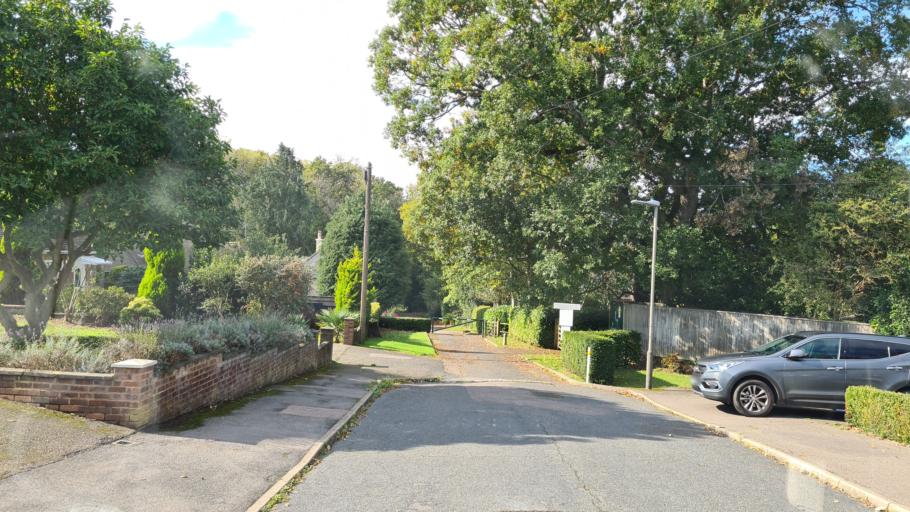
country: GB
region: England
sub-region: East Sussex
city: Hastings
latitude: 50.8811
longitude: 0.5675
